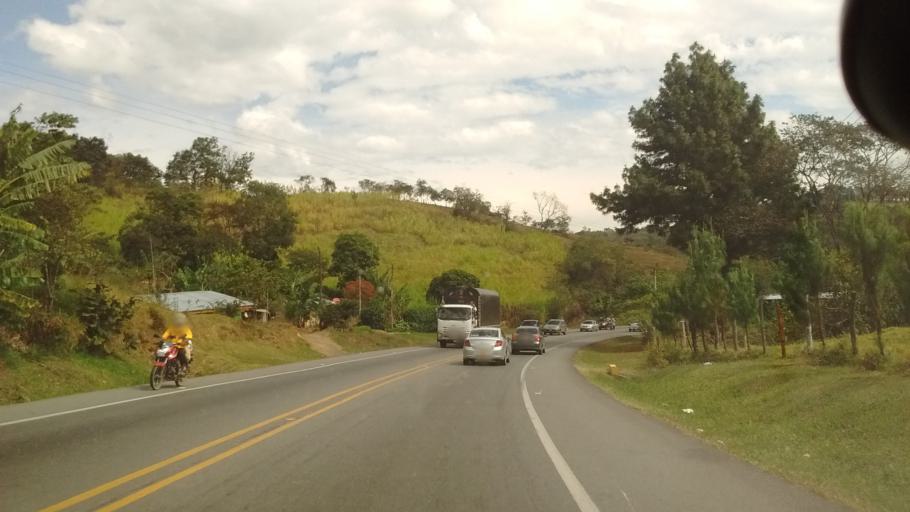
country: CO
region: Cauca
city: Cajibio
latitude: 2.6060
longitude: -76.5285
